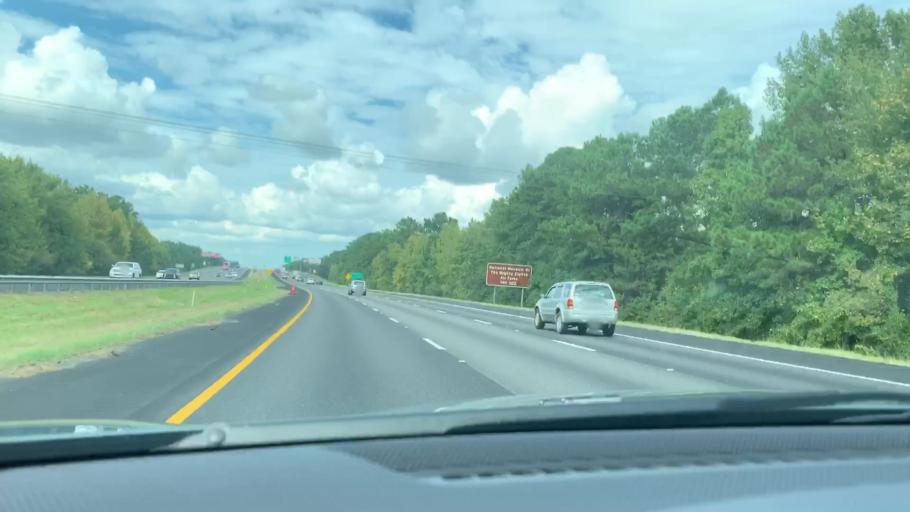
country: US
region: Georgia
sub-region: Chatham County
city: Pooler
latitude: 32.0959
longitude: -81.2364
